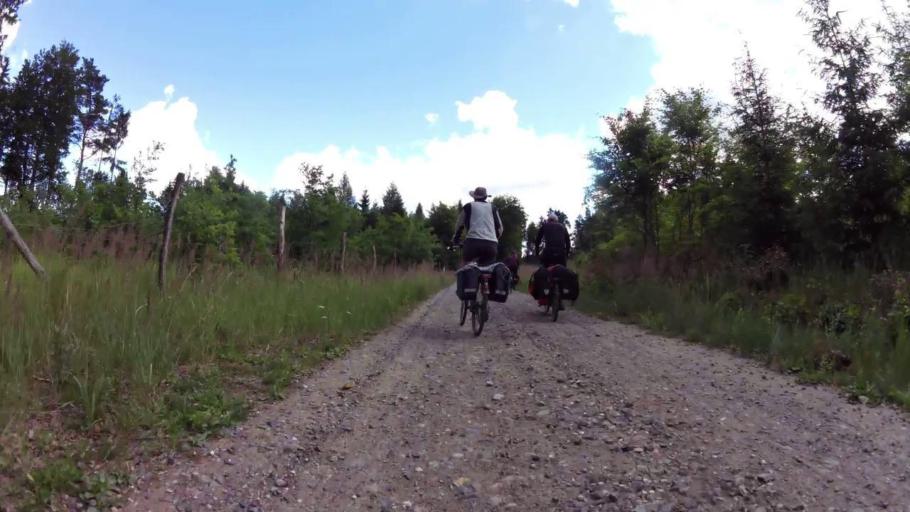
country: PL
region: West Pomeranian Voivodeship
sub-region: Powiat lobeski
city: Radowo Male
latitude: 53.7343
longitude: 15.5239
